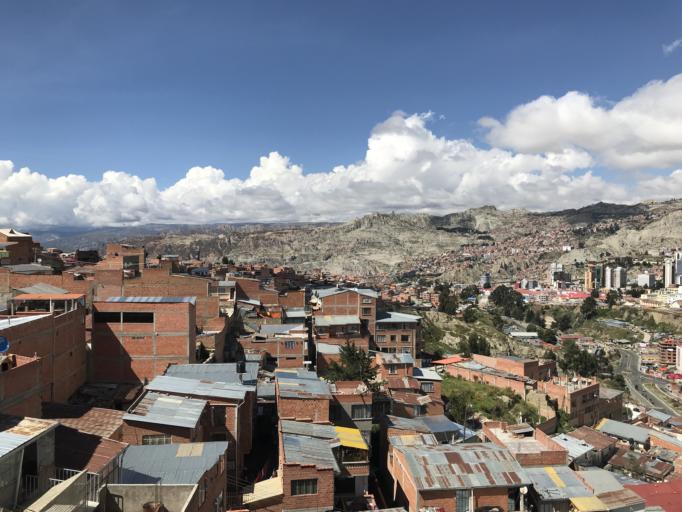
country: BO
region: La Paz
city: La Paz
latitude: -16.5014
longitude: -68.1127
